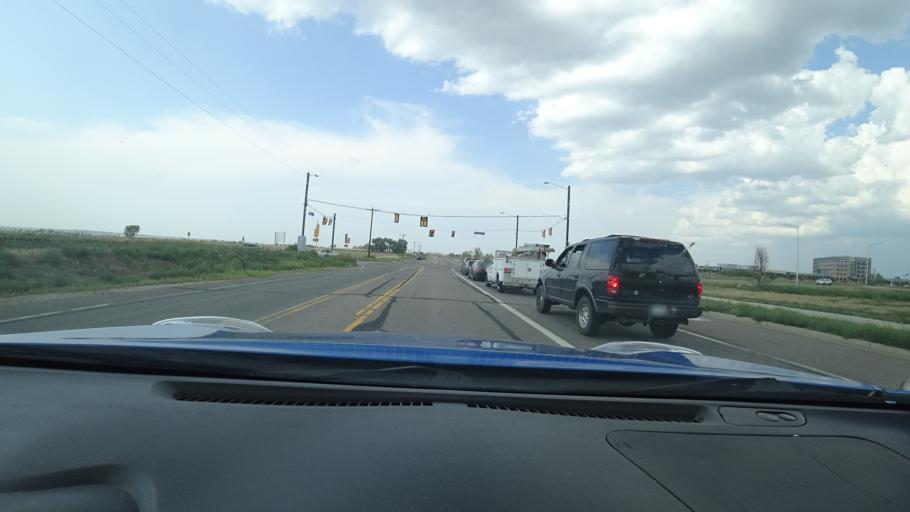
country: US
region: Colorado
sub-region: Adams County
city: Brighton
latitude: 39.9208
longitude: -104.8182
